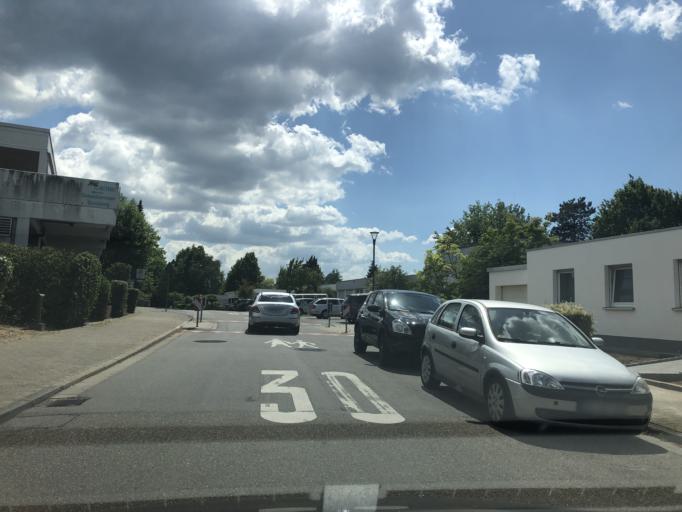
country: DE
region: Baden-Wuerttemberg
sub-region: Karlsruhe Region
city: Leimen
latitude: 49.3750
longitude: 8.7028
